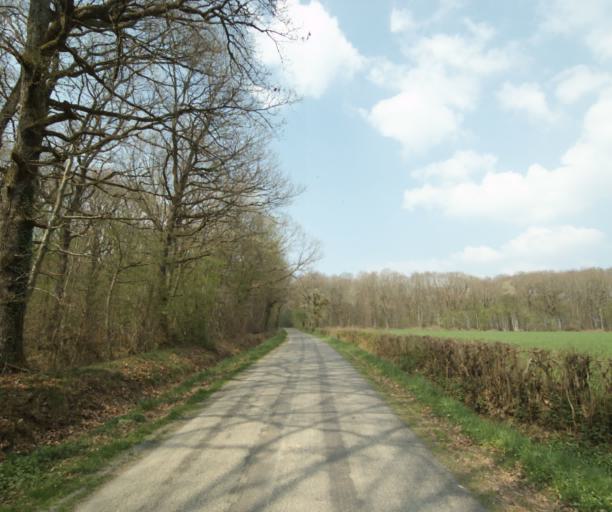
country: FR
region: Bourgogne
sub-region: Departement de Saone-et-Loire
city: Charolles
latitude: 46.4600
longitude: 4.3482
